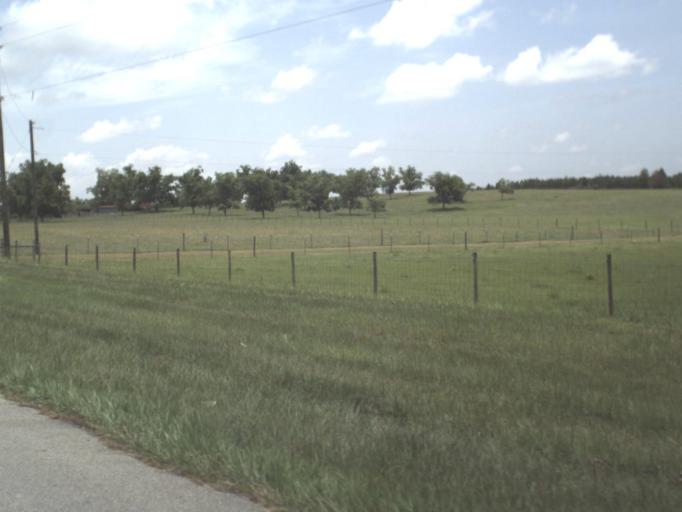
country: US
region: Florida
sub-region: Madison County
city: Madison
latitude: 30.5020
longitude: -83.4234
